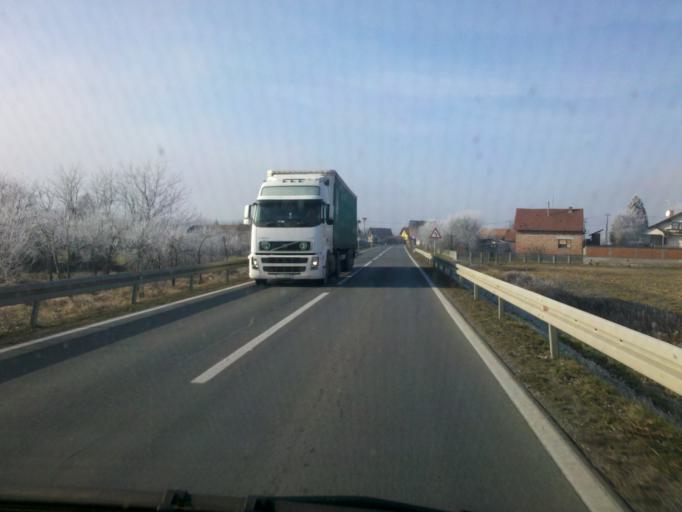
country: HR
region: Virovitick-Podravska
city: Pitomaca
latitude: 45.9678
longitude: 17.1992
